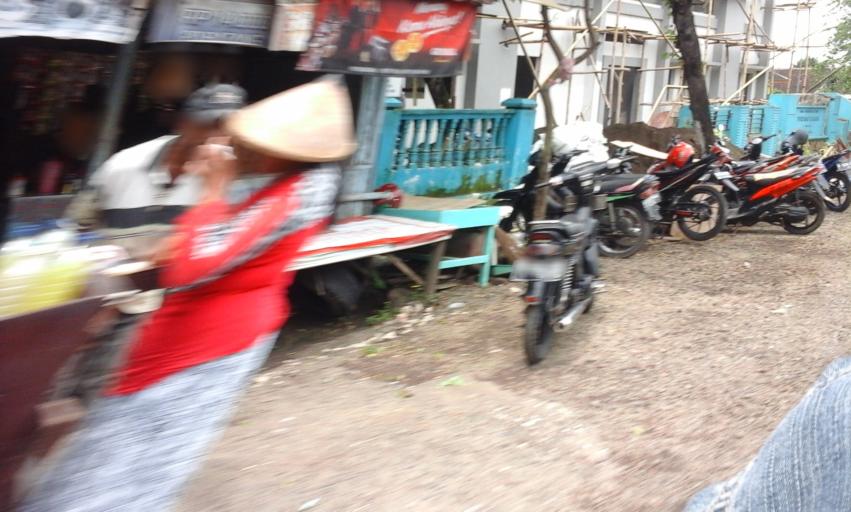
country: ID
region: East Java
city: Klatakan
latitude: -8.1876
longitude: 113.4897
